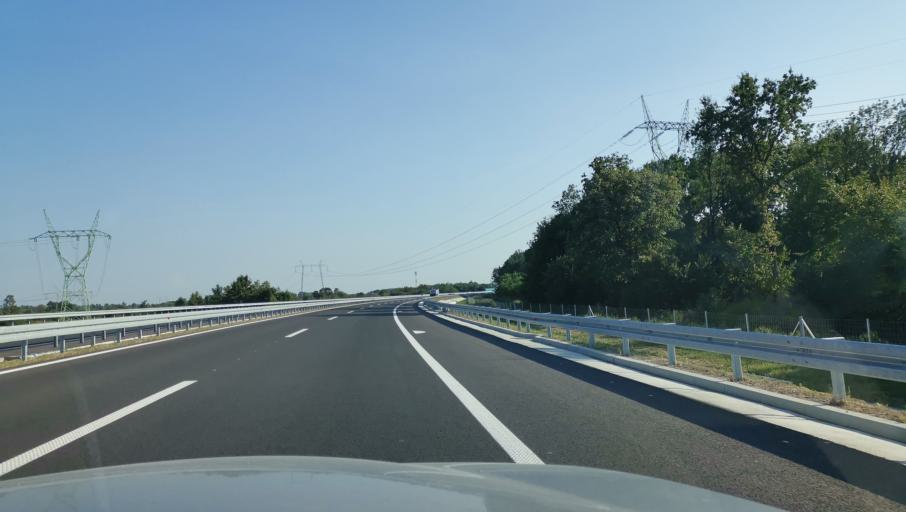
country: RS
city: Zvecka
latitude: 44.5995
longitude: 20.2001
